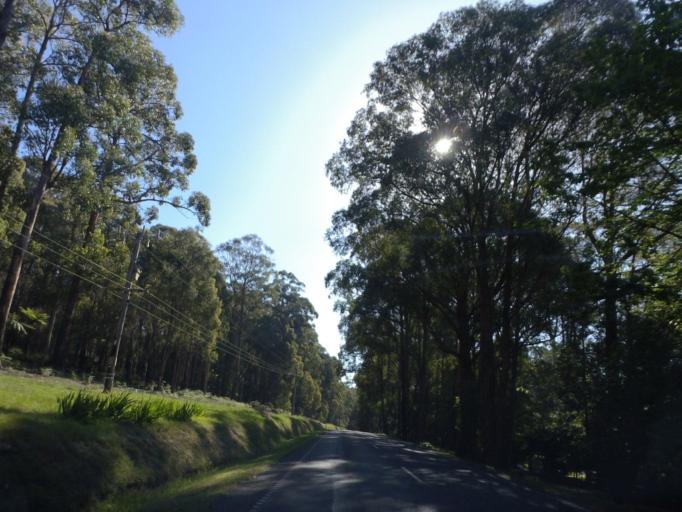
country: AU
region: Victoria
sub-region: Yarra Ranges
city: Millgrove
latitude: -37.8604
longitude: 145.7369
